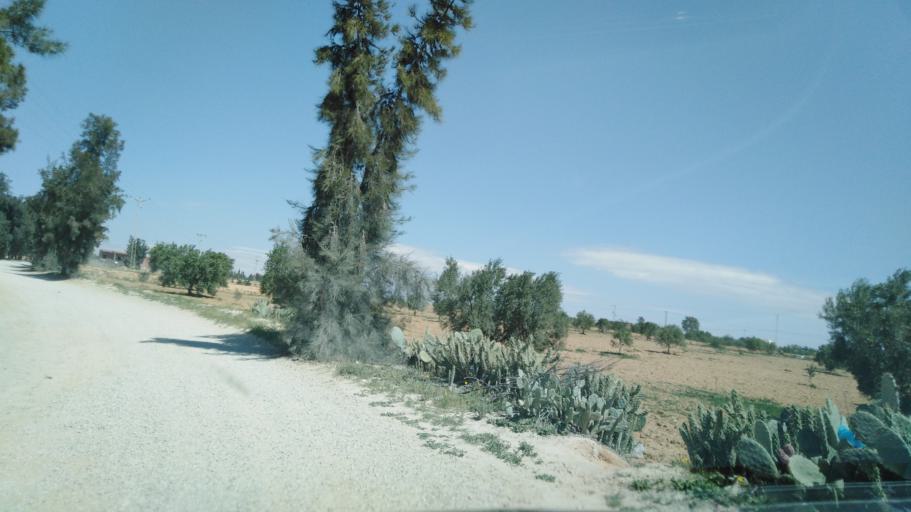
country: TN
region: Safaqis
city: Sfax
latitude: 34.7561
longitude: 10.5300
